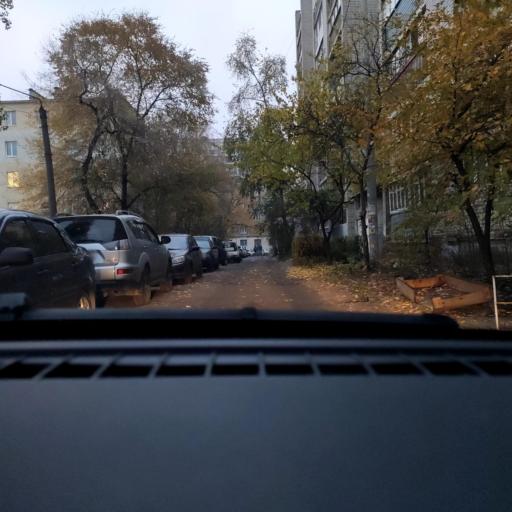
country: RU
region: Voronezj
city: Maslovka
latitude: 51.6340
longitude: 39.2805
